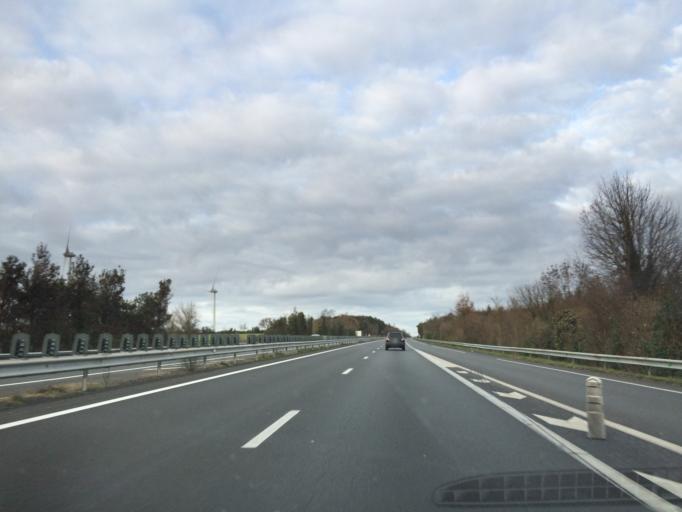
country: FR
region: Poitou-Charentes
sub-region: Departement de la Charente-Maritime
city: Saint-Jean-d'Angely
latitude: 46.0136
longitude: -0.5411
